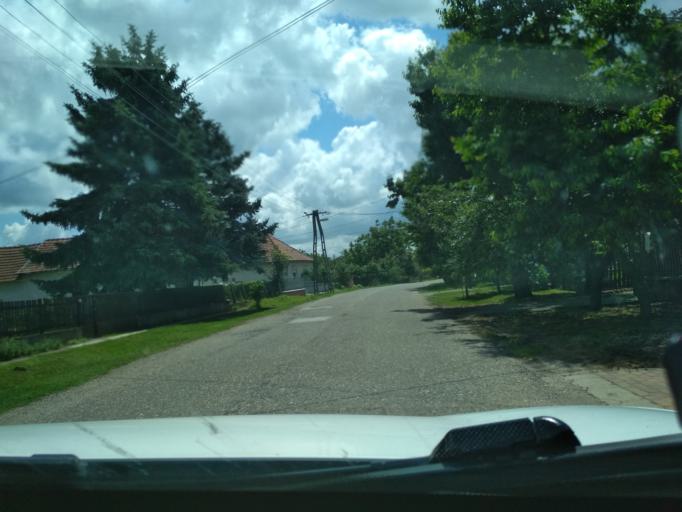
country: HU
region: Jasz-Nagykun-Szolnok
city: Tiszafured
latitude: 47.6095
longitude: 20.7755
